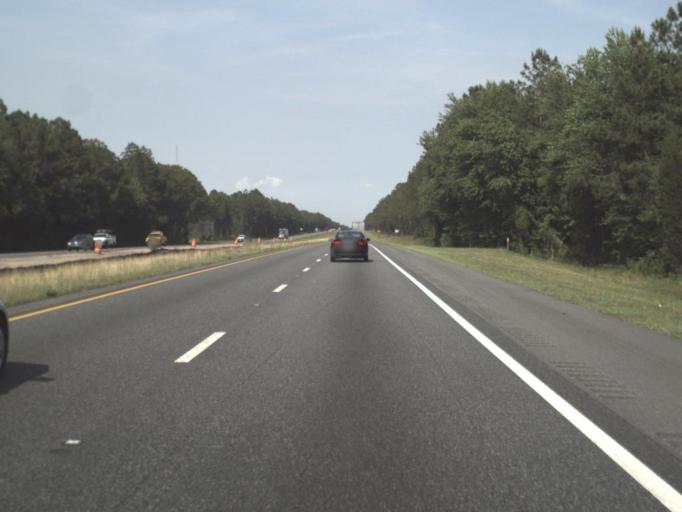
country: US
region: Florida
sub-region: Baker County
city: Macclenny
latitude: 30.2695
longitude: -82.0886
